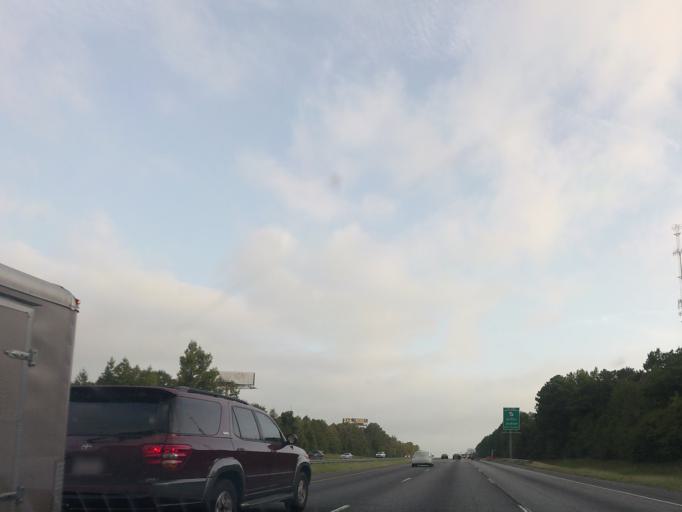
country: US
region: Georgia
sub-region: Henry County
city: Locust Grove
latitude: 33.2515
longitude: -84.0884
